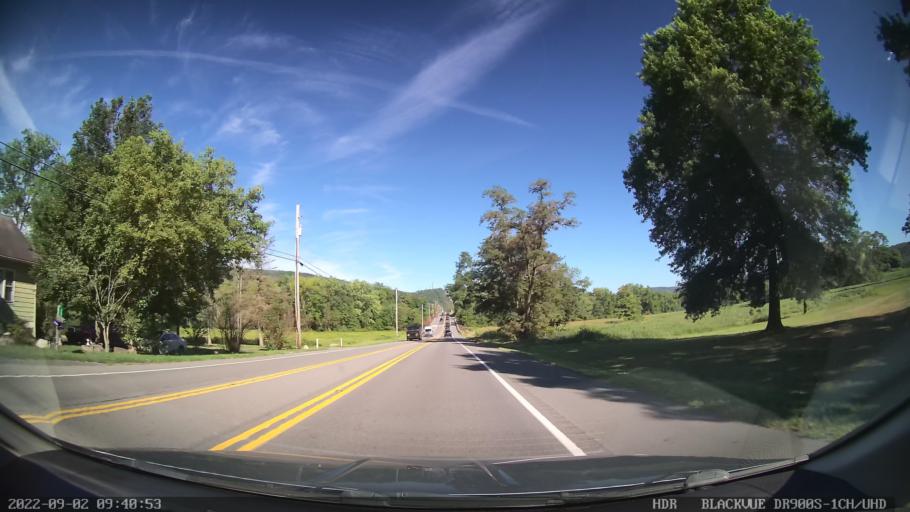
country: US
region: Pennsylvania
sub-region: Montour County
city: Mechanicsville
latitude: 40.9312
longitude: -76.5927
